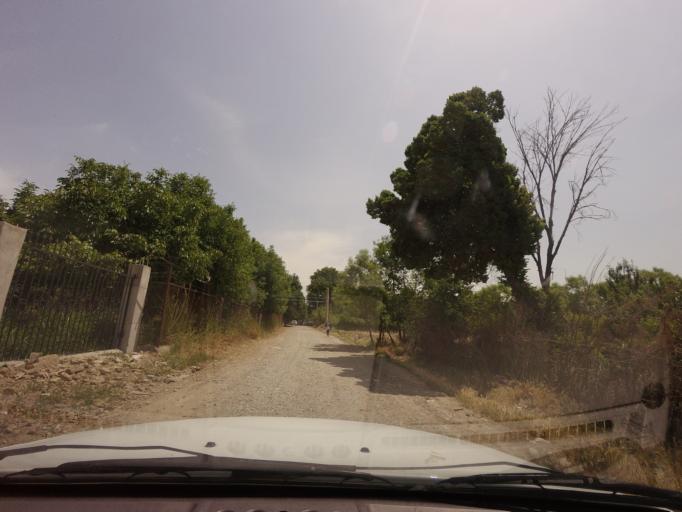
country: IR
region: Tehran
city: Eslamshahr
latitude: 35.6366
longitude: 51.2425
